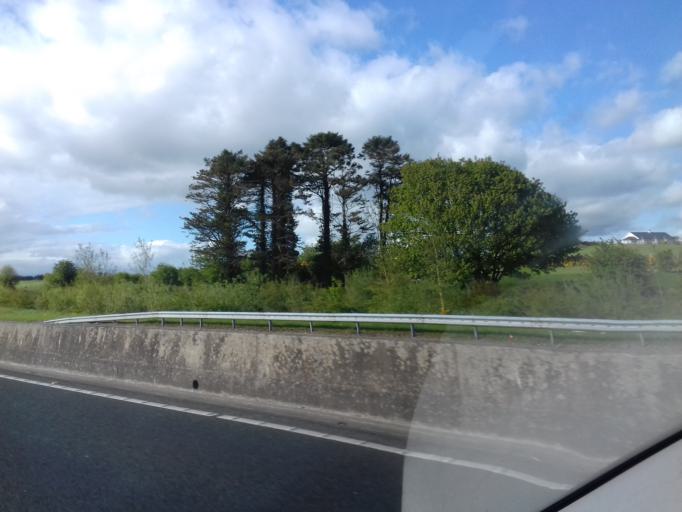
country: IE
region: Leinster
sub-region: Kilkenny
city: Mooncoin
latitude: 52.4163
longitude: -7.2203
